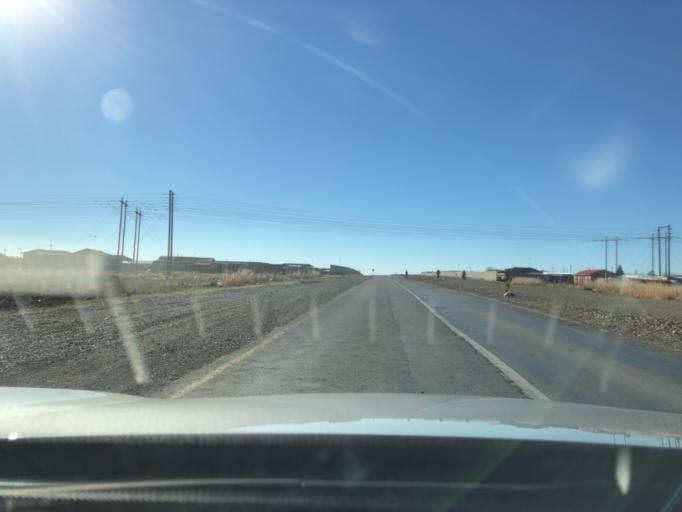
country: ZA
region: Mpumalanga
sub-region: Gert Sibande District Municipality
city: Standerton
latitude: -26.9396
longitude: 29.2006
